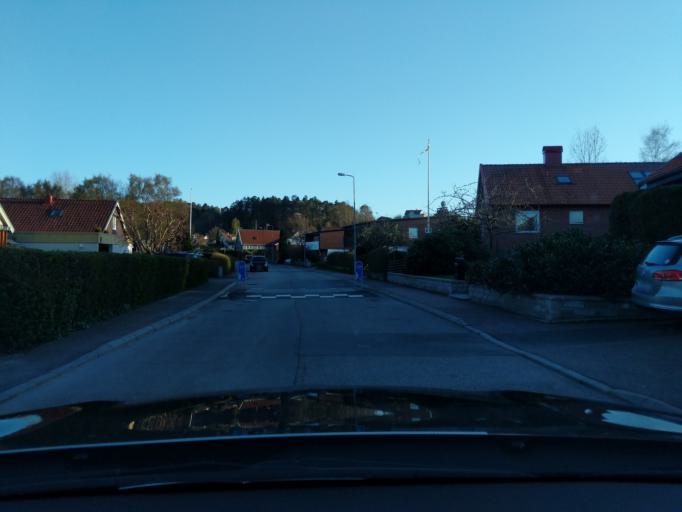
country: SE
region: Vaestra Goetaland
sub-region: Goteborg
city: Majorna
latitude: 57.6368
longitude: 11.9292
